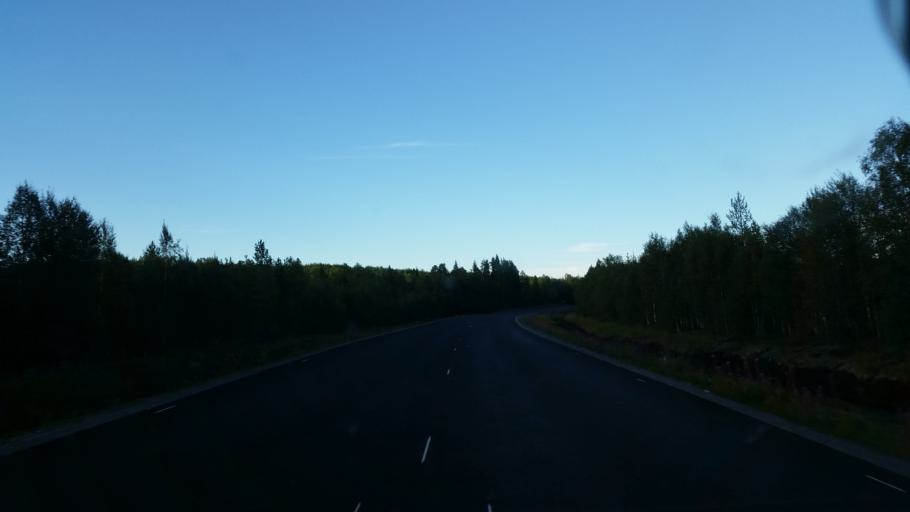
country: SE
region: Vaesterbotten
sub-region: Dorotea Kommun
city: Dorotea
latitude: 64.2984
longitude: 16.5544
